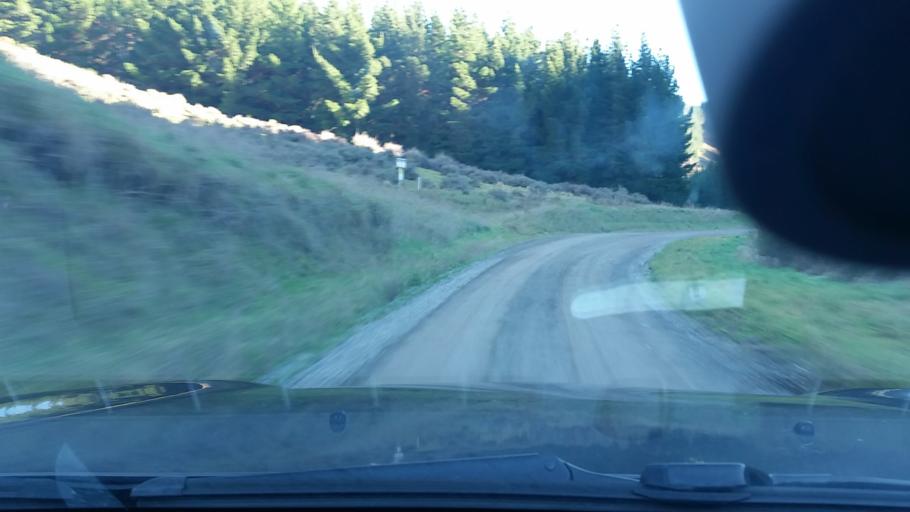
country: NZ
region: Marlborough
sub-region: Marlborough District
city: Blenheim
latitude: -41.6105
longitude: 173.9732
